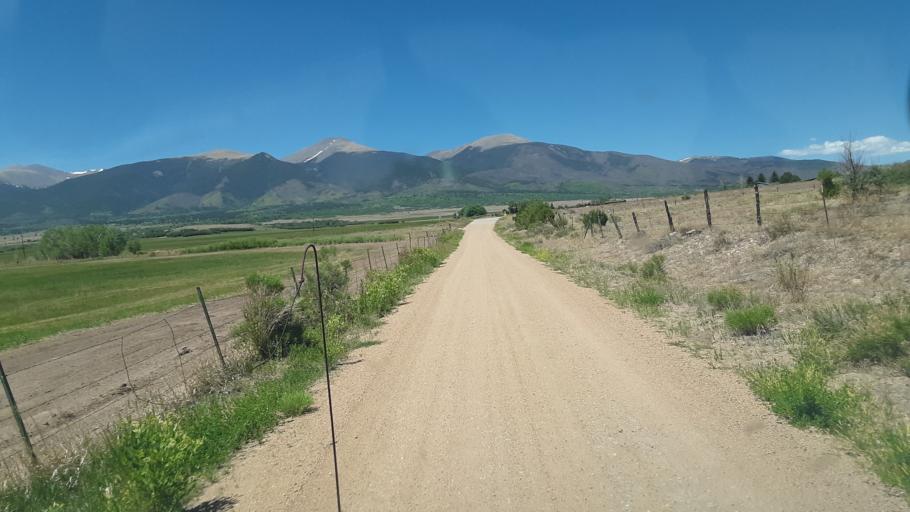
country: US
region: Colorado
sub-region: Custer County
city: Westcliffe
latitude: 38.2934
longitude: -105.6188
